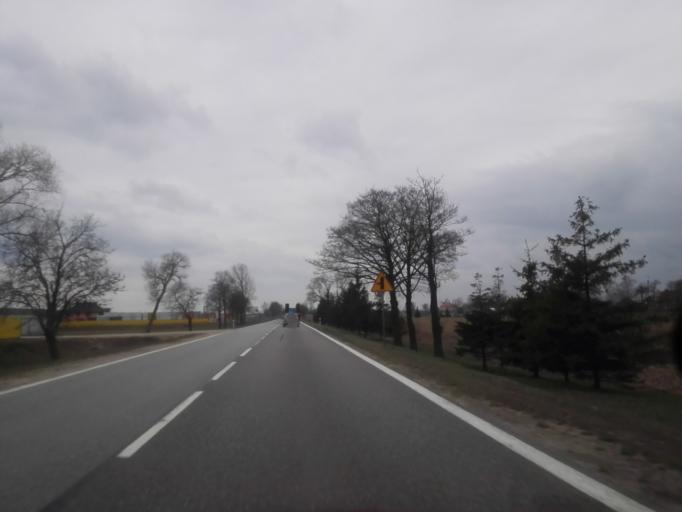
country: PL
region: Podlasie
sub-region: Powiat augustowski
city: Augustow
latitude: 53.8223
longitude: 22.9380
